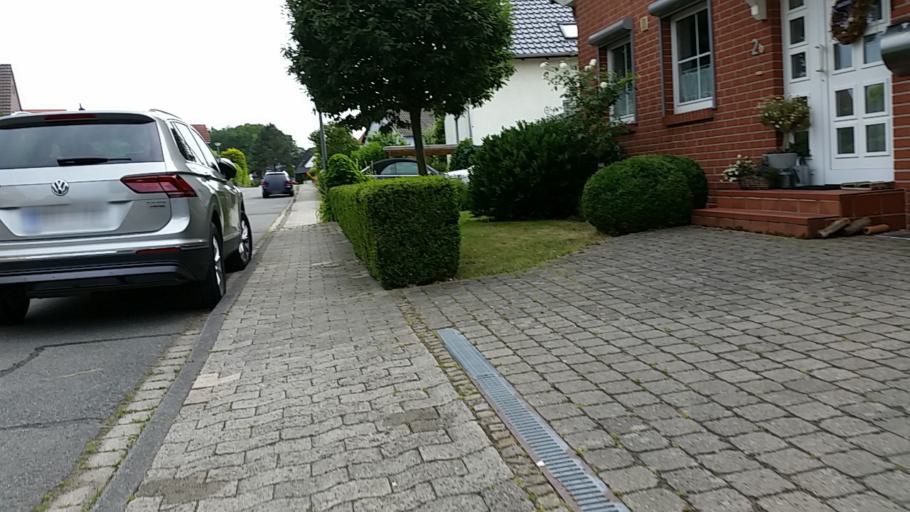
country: DE
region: Lower Saxony
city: Weyhausen
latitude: 52.3945
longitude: 10.7069
